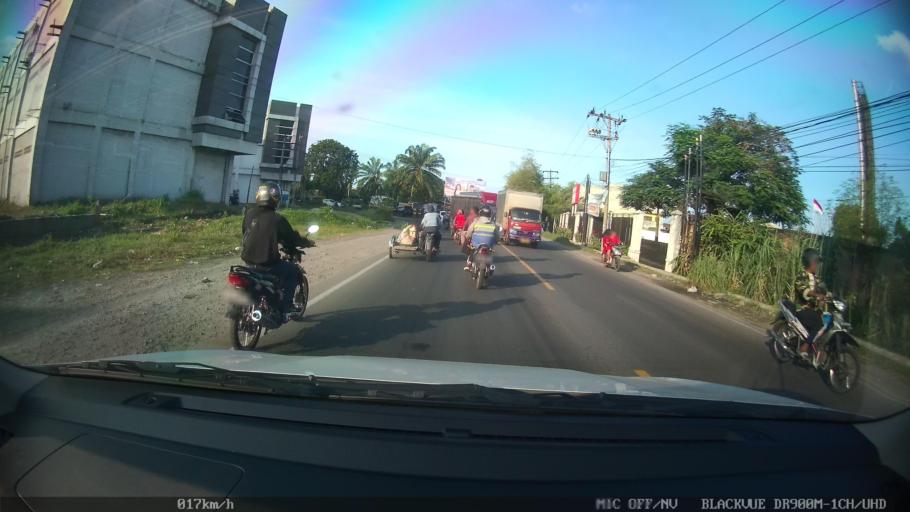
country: ID
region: North Sumatra
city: Medan
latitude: 3.6224
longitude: 98.6596
